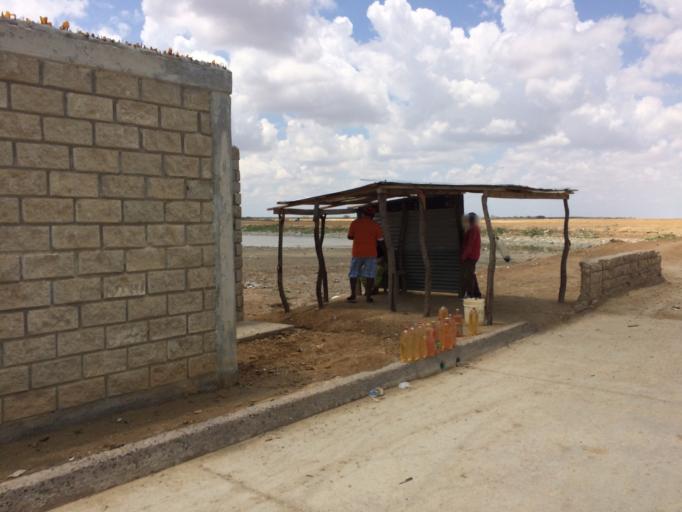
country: CO
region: La Guajira
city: Manaure
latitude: 11.7727
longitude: -72.4488
